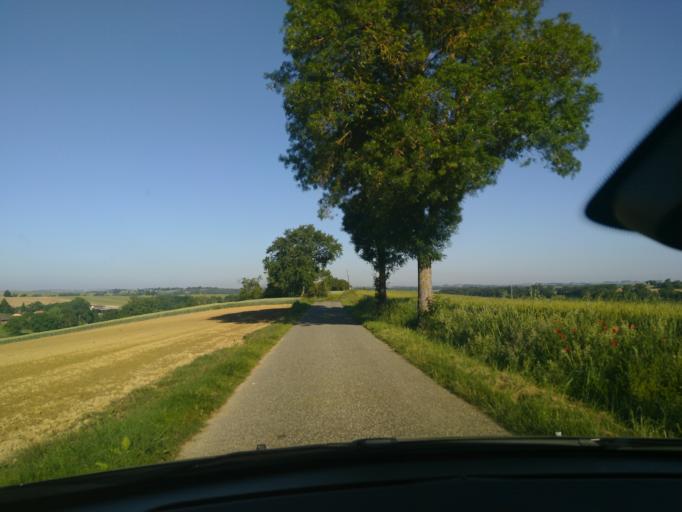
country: FR
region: Midi-Pyrenees
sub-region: Departement du Tarn-et-Garonne
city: Beaumont-de-Lomagne
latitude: 43.7776
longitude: 0.9521
